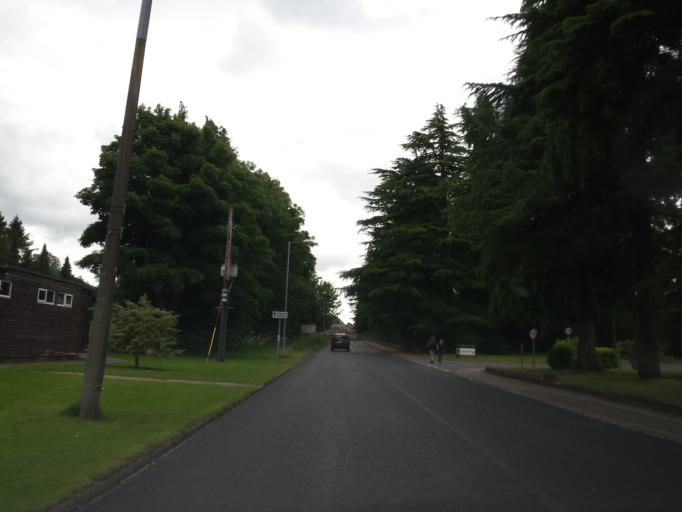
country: GB
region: Scotland
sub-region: Dumfries and Galloway
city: Dumfries
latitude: 55.0550
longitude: -3.5952
